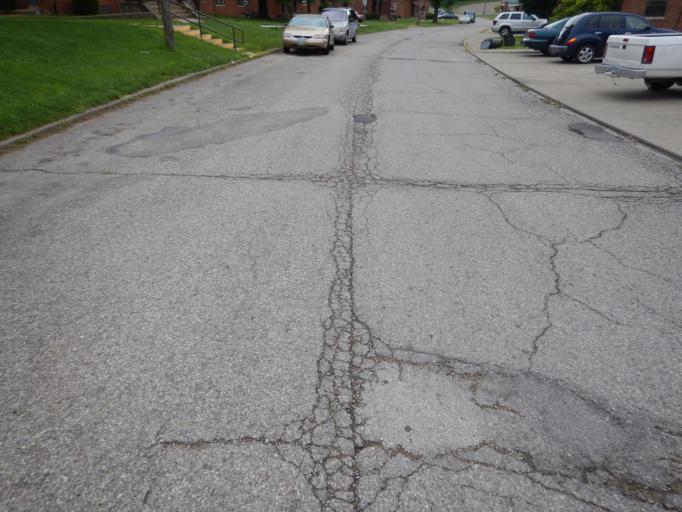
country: US
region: Ohio
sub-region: Muskingum County
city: Zanesville
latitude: 39.9271
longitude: -82.0113
